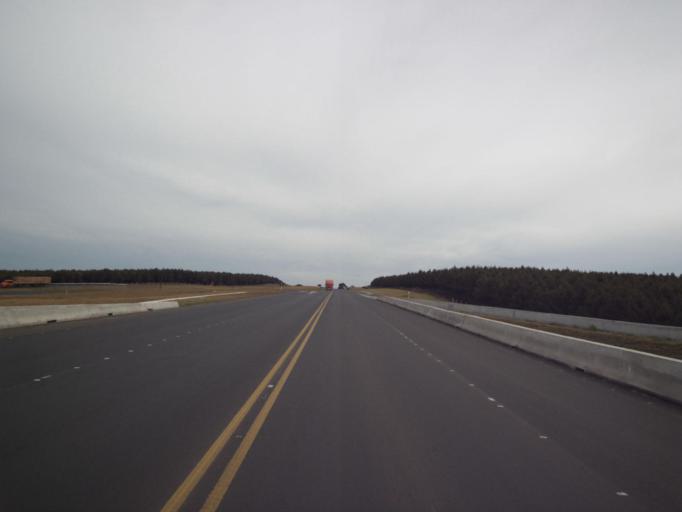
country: BR
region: Santa Catarina
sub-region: Cacador
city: Cacador
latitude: -26.6094
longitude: -51.4800
